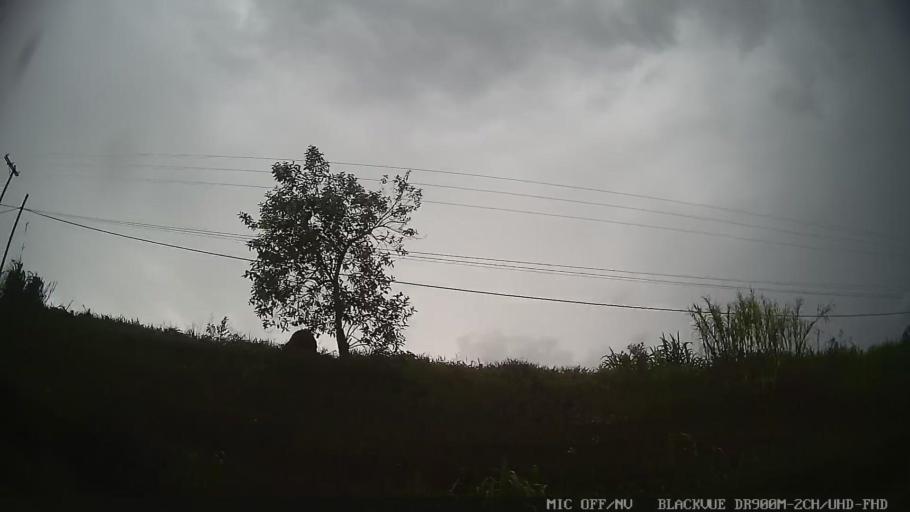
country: BR
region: Sao Paulo
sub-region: Pedreira
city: Pedreira
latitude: -22.6983
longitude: -46.8720
